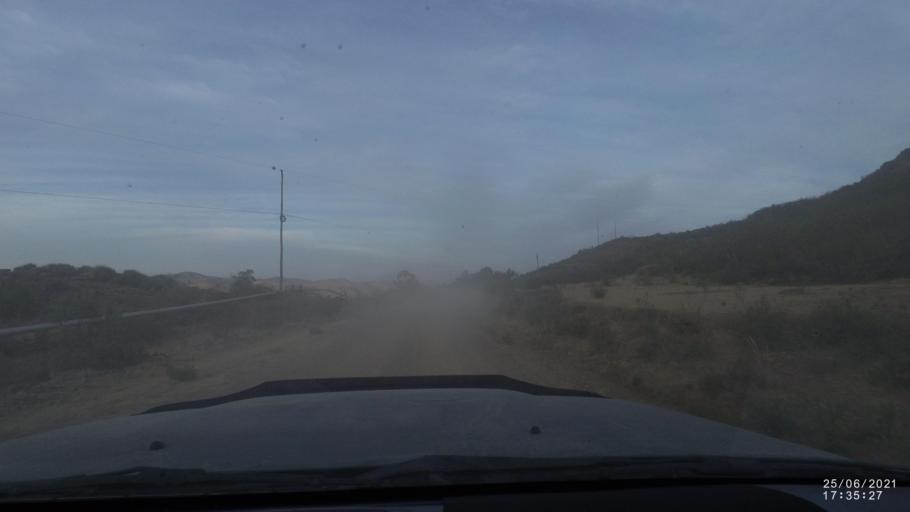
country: BO
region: Cochabamba
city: Mizque
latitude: -17.9503
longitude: -65.6540
